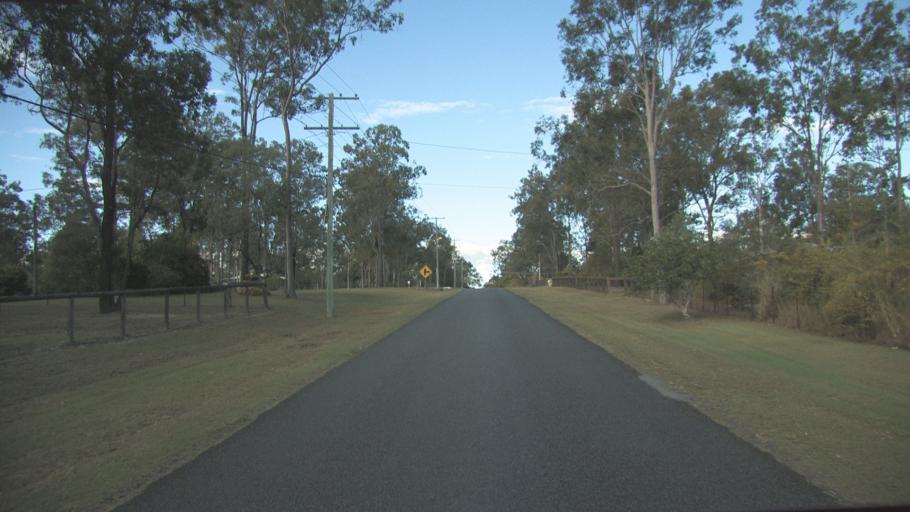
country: AU
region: Queensland
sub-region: Logan
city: North Maclean
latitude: -27.8183
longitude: 153.0514
